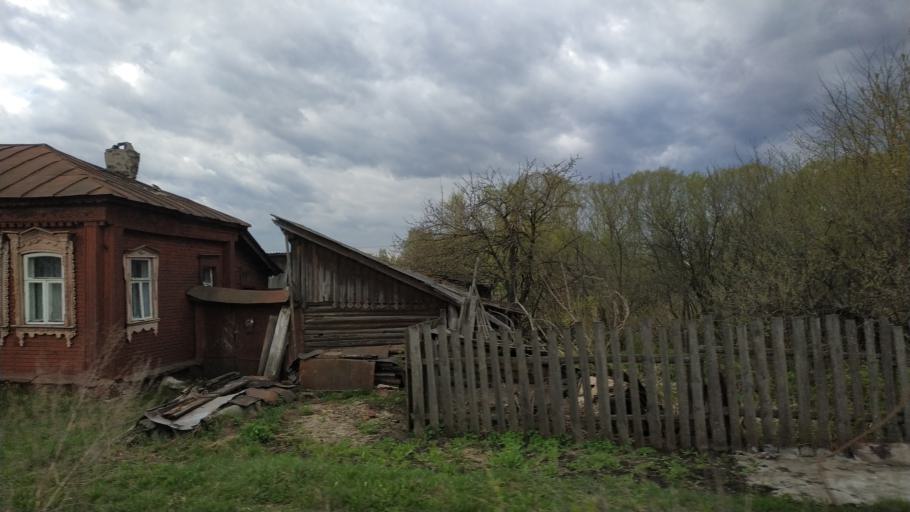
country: RU
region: Moskovskaya
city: Pavlovskiy Posad
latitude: 55.7870
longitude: 38.6865
